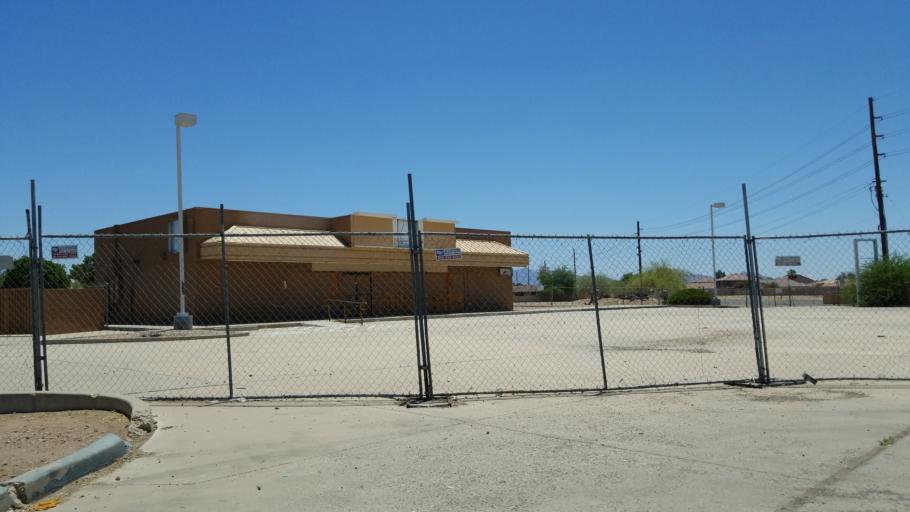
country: US
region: Arizona
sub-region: Maricopa County
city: Tolleson
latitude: 33.5087
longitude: -112.2549
